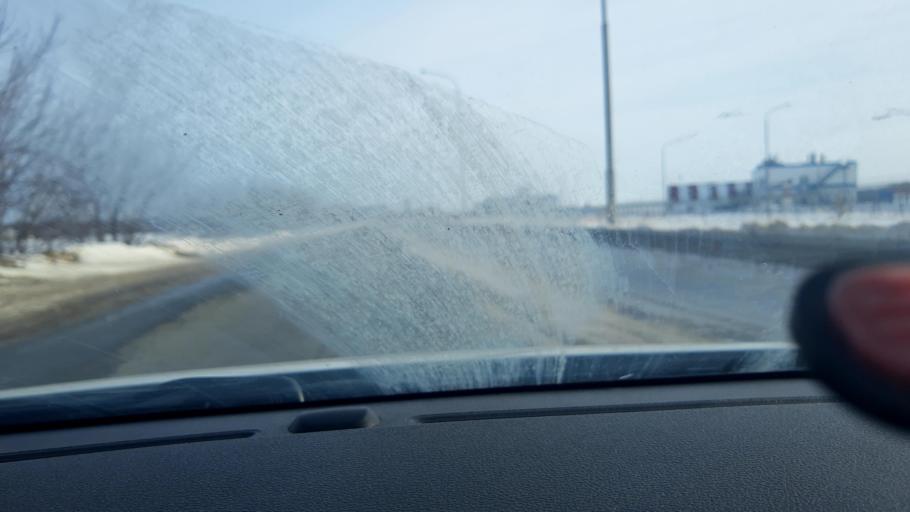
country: RU
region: Bashkortostan
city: Avdon
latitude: 54.5787
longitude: 55.8665
